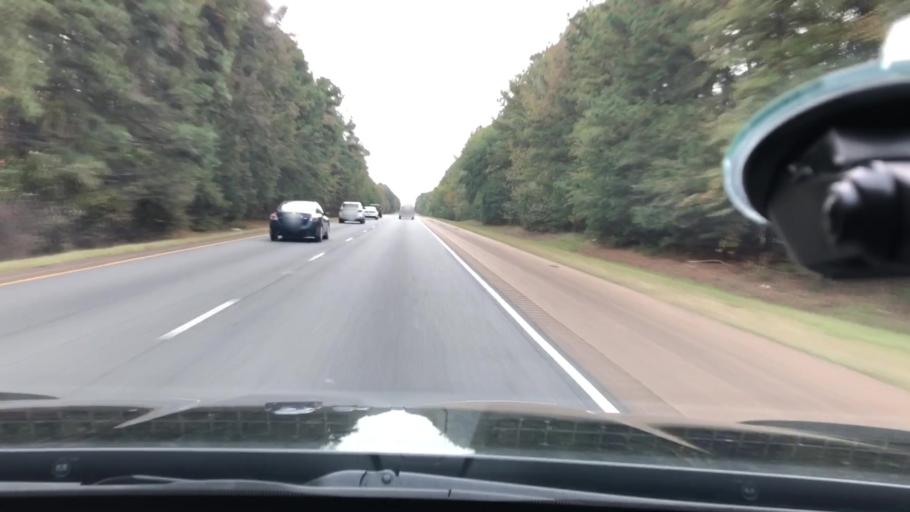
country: US
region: Arkansas
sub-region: Nevada County
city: Prescott
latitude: 33.8582
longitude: -93.3578
